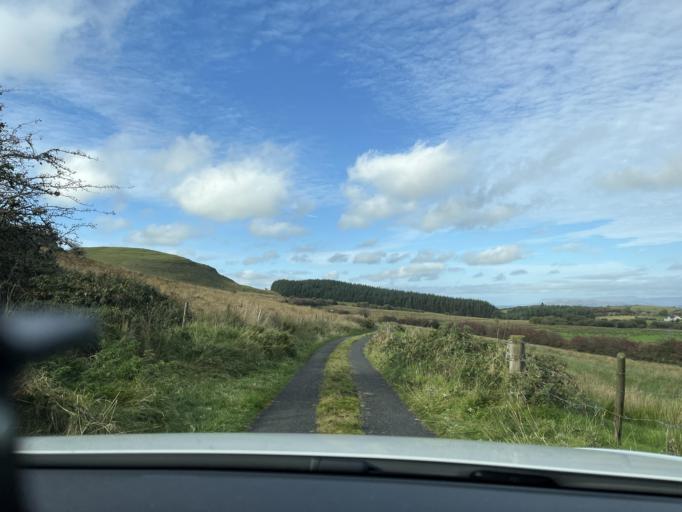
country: IE
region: Connaught
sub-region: Sligo
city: Ballymote
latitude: 54.0630
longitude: -8.4245
